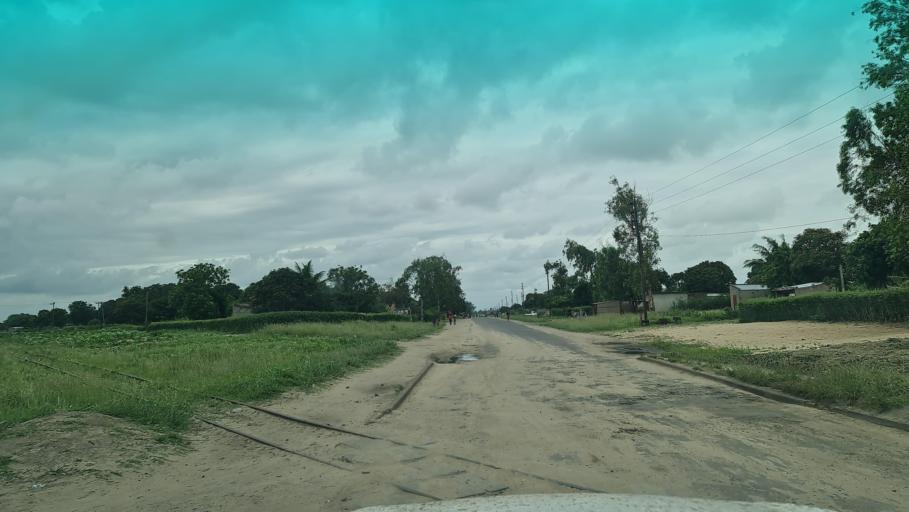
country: MZ
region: Maputo
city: Manhica
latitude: -25.4442
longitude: 32.7737
